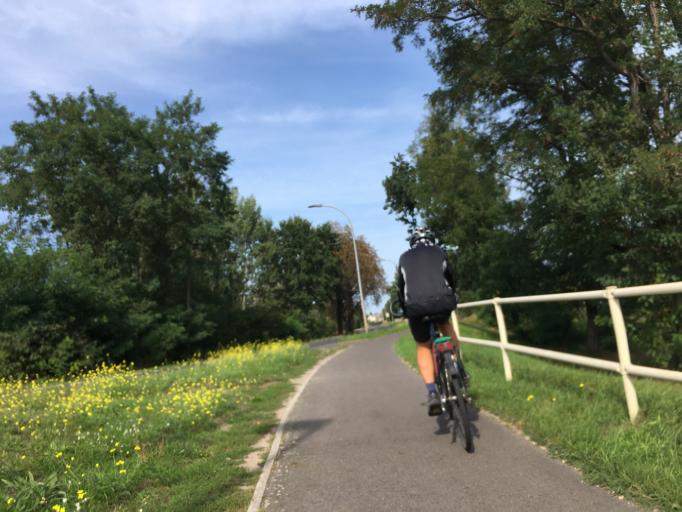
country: DE
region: Brandenburg
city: Guben
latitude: 51.9709
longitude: 14.7016
